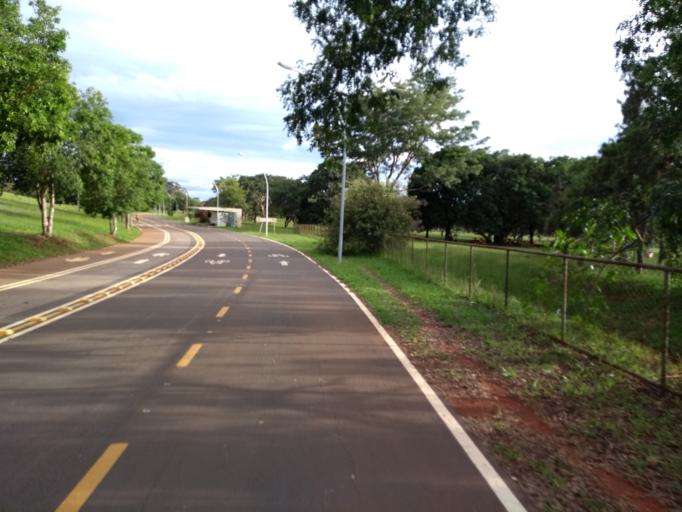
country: BR
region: Federal District
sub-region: Brasilia
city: Brasilia
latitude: -15.8051
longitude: -47.9164
